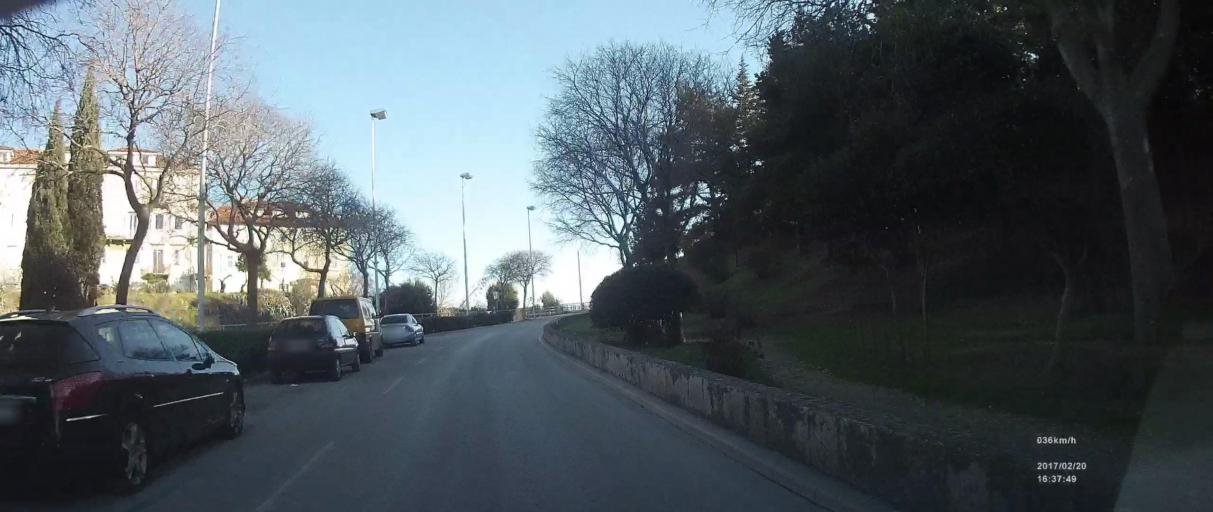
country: HR
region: Splitsko-Dalmatinska
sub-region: Grad Split
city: Split
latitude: 43.5024
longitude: 16.4439
